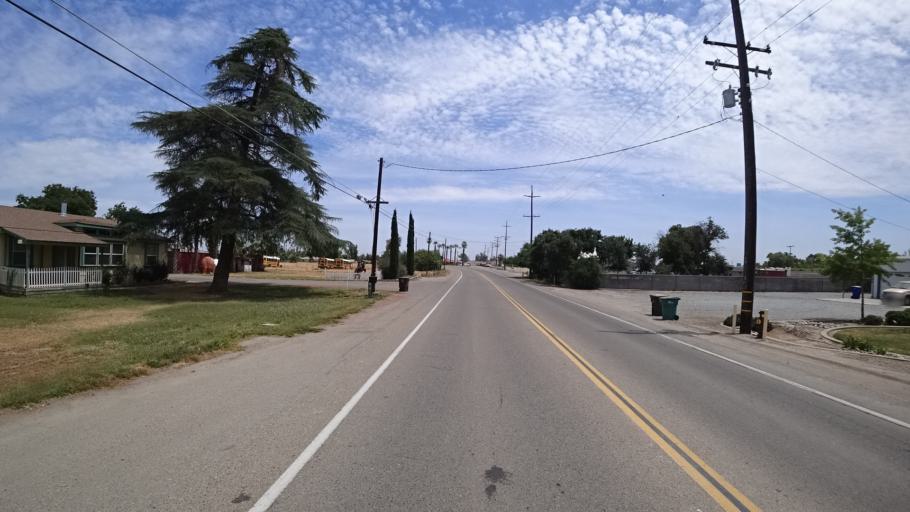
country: US
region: California
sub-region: Kings County
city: Armona
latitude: 36.3136
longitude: -119.6997
